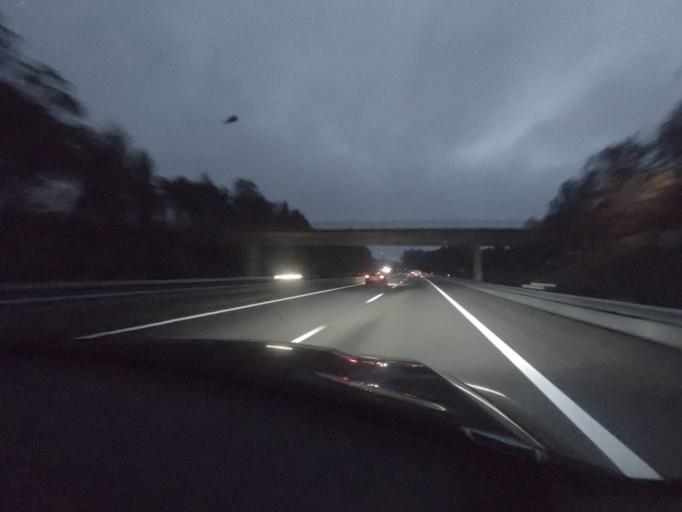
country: PT
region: Leiria
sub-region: Leiria
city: Caranguejeira
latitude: 39.8028
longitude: -8.7249
